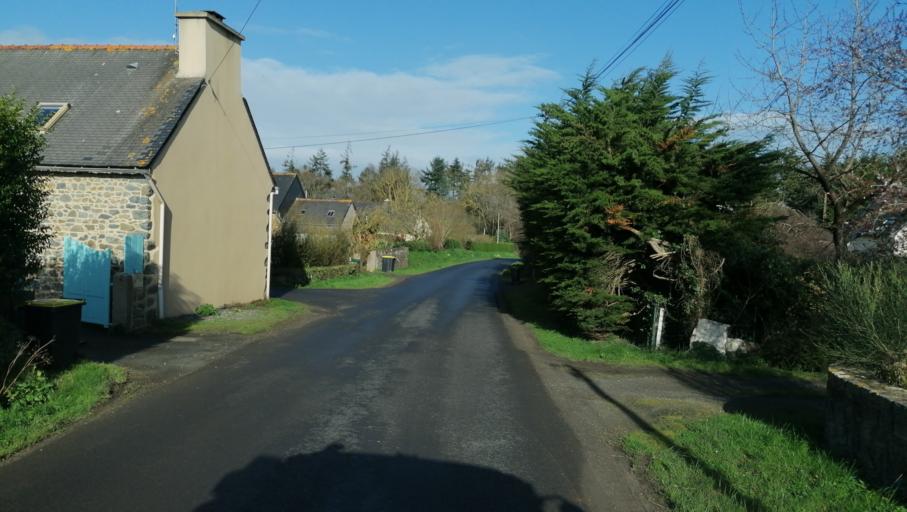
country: FR
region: Brittany
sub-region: Departement des Cotes-d'Armor
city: Plouha
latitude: 48.6477
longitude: -2.9040
